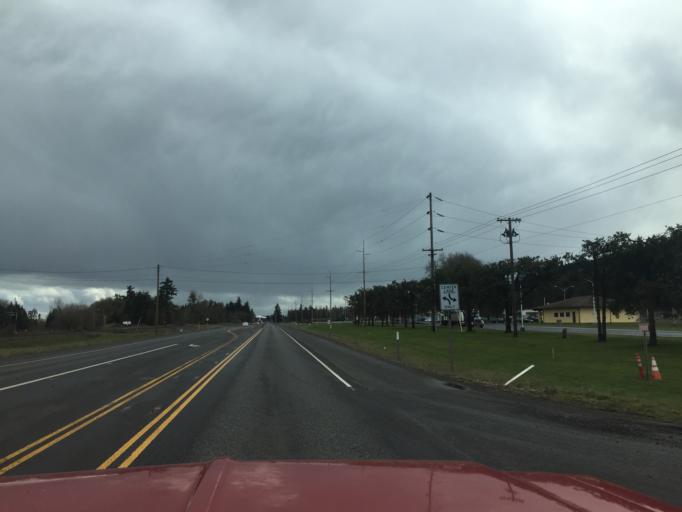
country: US
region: Oregon
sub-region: Columbia County
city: Columbia City
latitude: 45.9140
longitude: -122.8268
